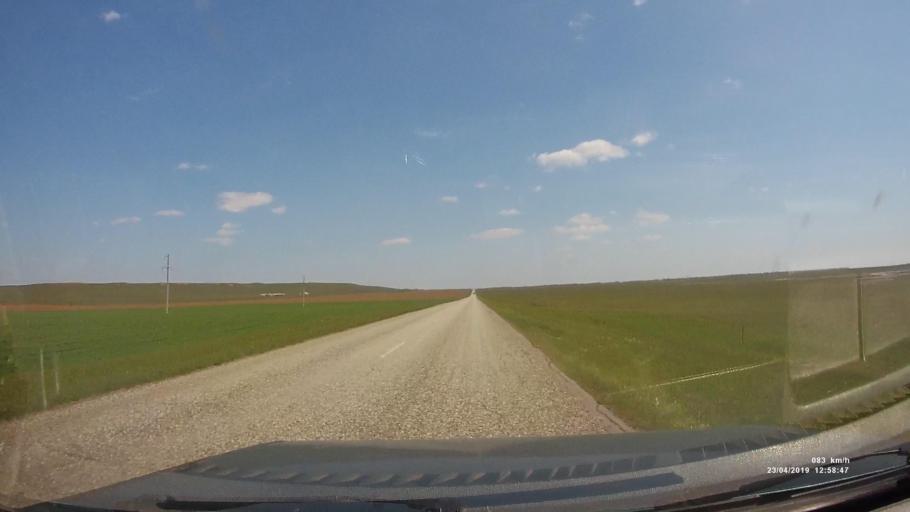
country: RU
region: Kalmykiya
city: Yashalta
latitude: 46.6044
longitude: 42.6028
